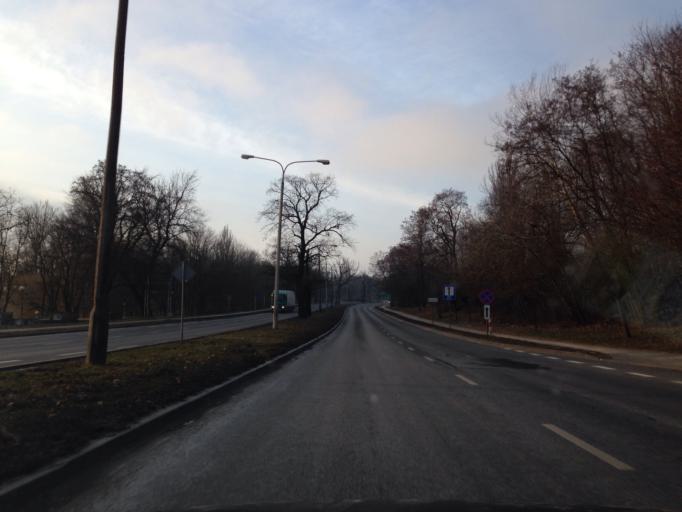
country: PL
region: Greater Poland Voivodeship
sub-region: Powiat gnieznienski
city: Gniezno
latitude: 52.5375
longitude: 17.5874
